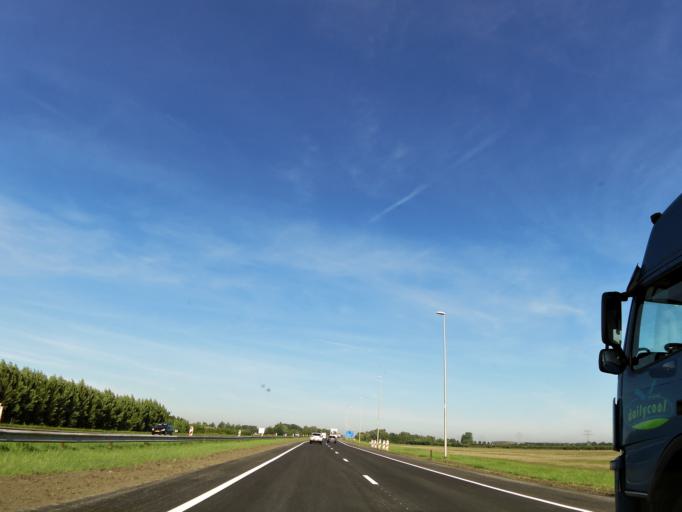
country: NL
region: Zeeland
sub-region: Gemeente Reimerswaal
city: Yerseke
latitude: 51.4300
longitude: 4.0795
